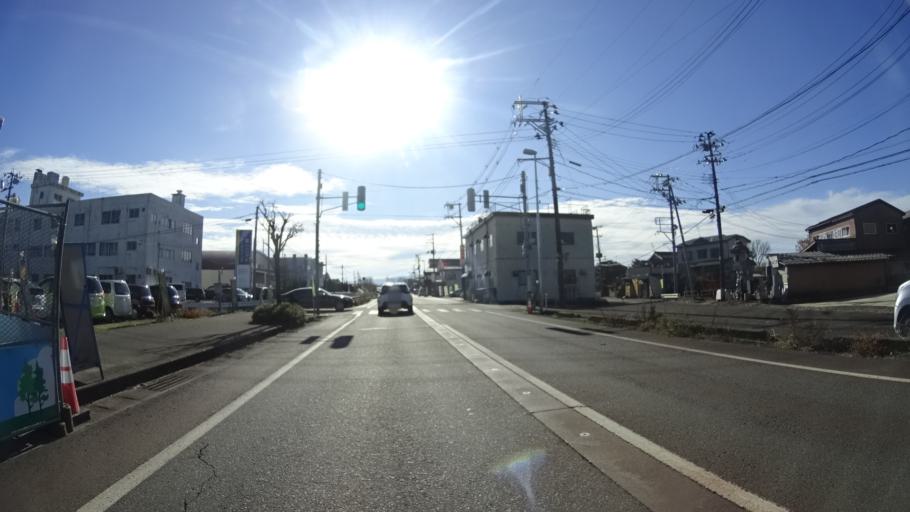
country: JP
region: Niigata
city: Mitsuke
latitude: 37.5401
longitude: 138.9007
